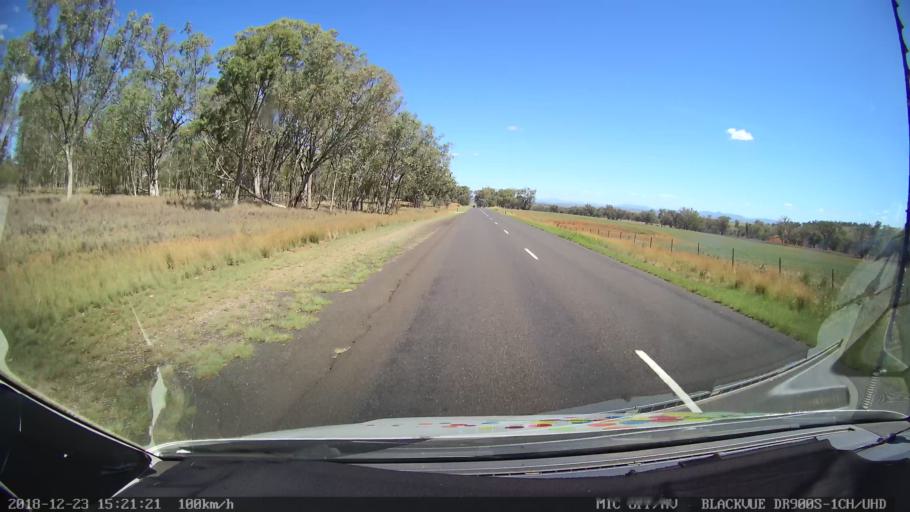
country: AU
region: New South Wales
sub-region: Tamworth Municipality
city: Manilla
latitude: -30.8551
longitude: 150.7960
